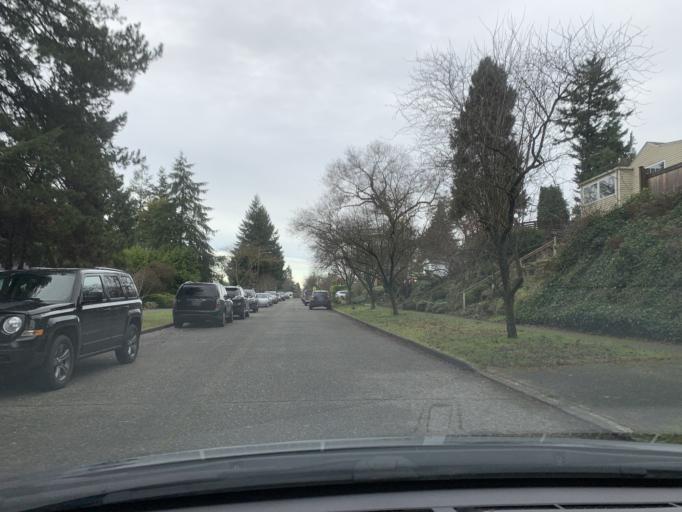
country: US
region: Washington
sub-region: King County
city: White Center
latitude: 47.5703
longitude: -122.3921
